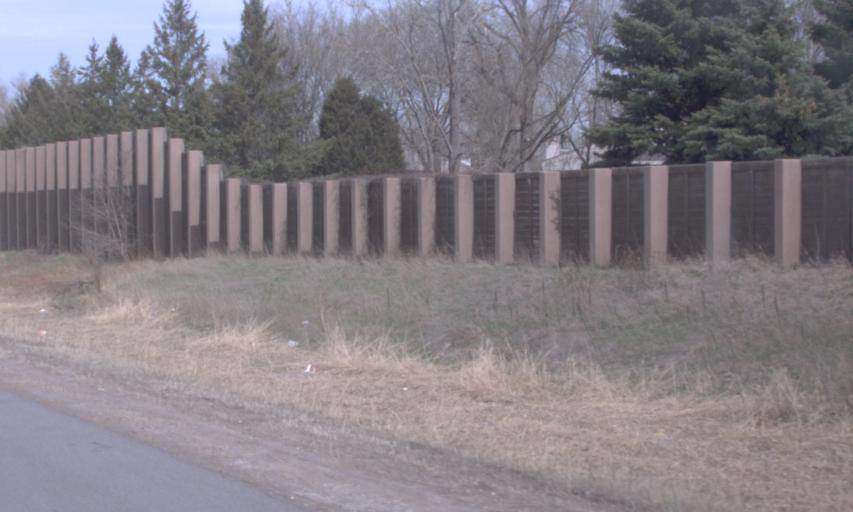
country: US
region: Minnesota
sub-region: Anoka County
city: Coon Rapids
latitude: 45.1617
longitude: -93.2836
